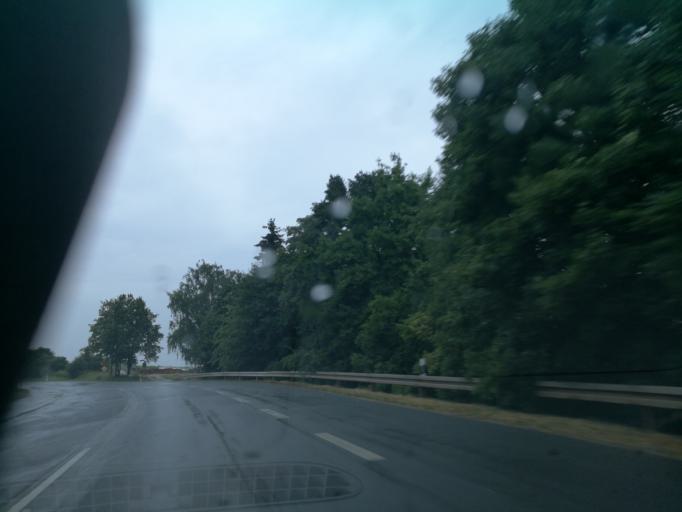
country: DE
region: Bavaria
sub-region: Regierungsbezirk Mittelfranken
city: Obermichelbach
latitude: 49.5319
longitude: 10.9609
